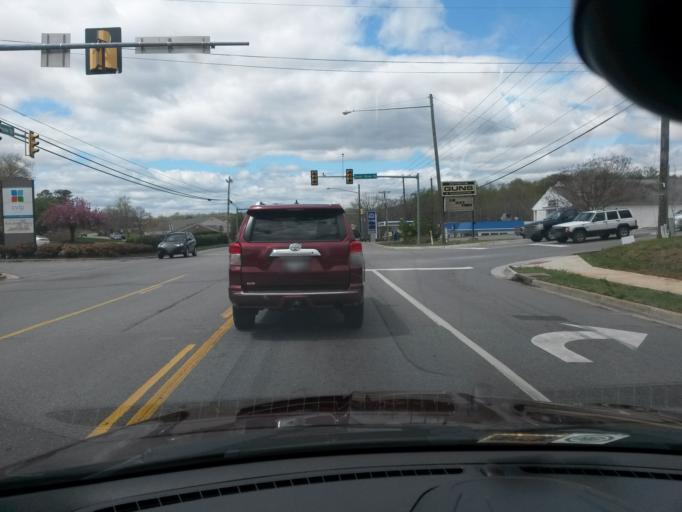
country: US
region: Virginia
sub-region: City of Lynchburg
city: West Lynchburg
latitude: 37.3995
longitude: -79.2069
